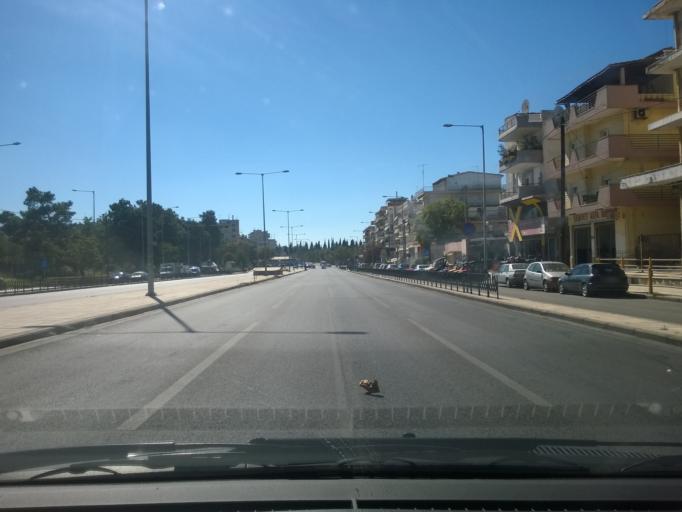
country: GR
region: Central Macedonia
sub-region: Nomos Thessalonikis
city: Ampelokipoi
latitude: 40.6585
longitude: 22.9348
